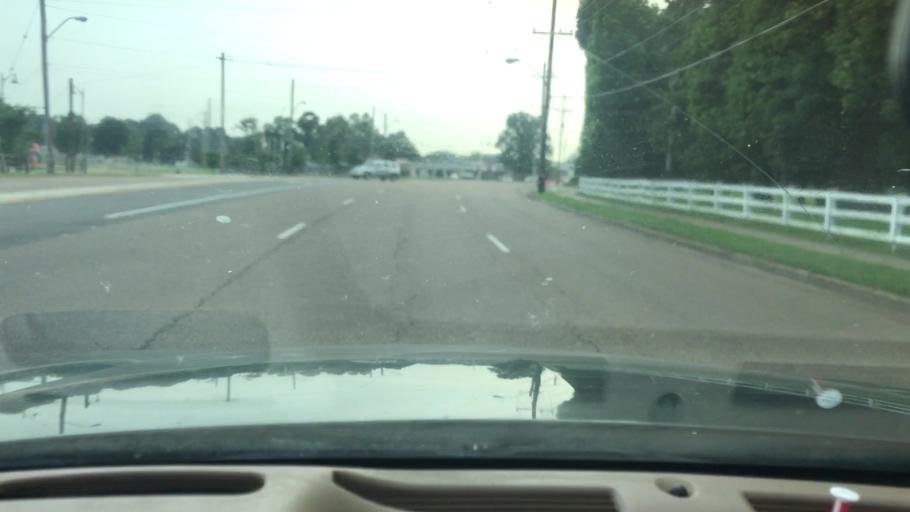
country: US
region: Tennessee
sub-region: Shelby County
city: Bartlett
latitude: 35.1987
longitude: -89.8688
